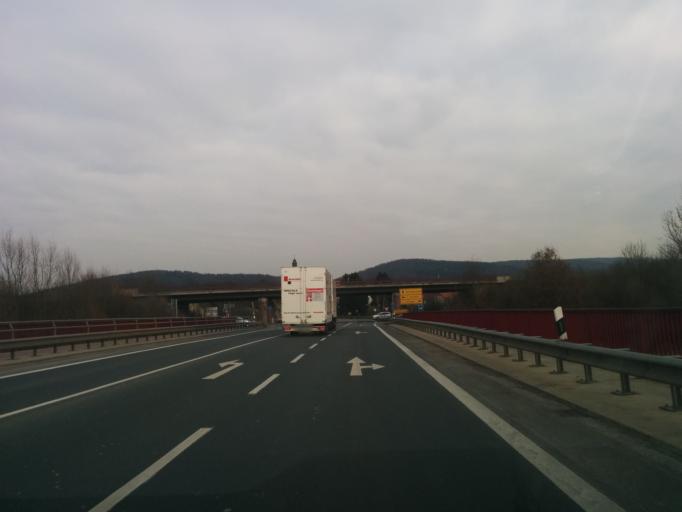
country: DE
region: Lower Saxony
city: Norten-Hardenberg
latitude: 51.6274
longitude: 9.9260
